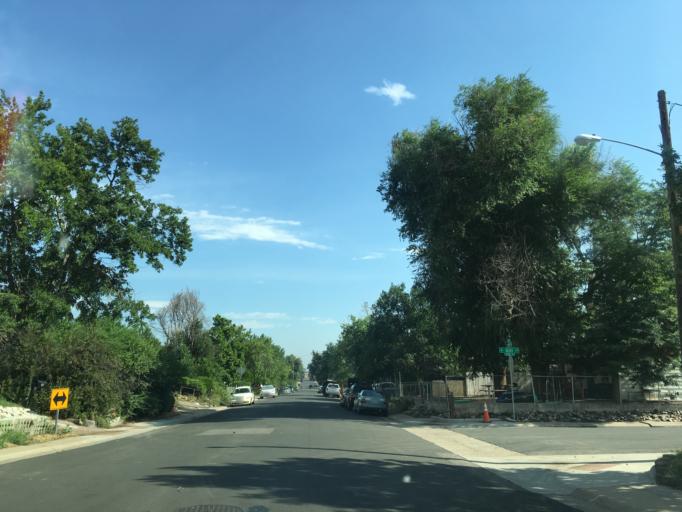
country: US
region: Colorado
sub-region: Jefferson County
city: Lakewood
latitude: 39.7047
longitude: -105.0350
